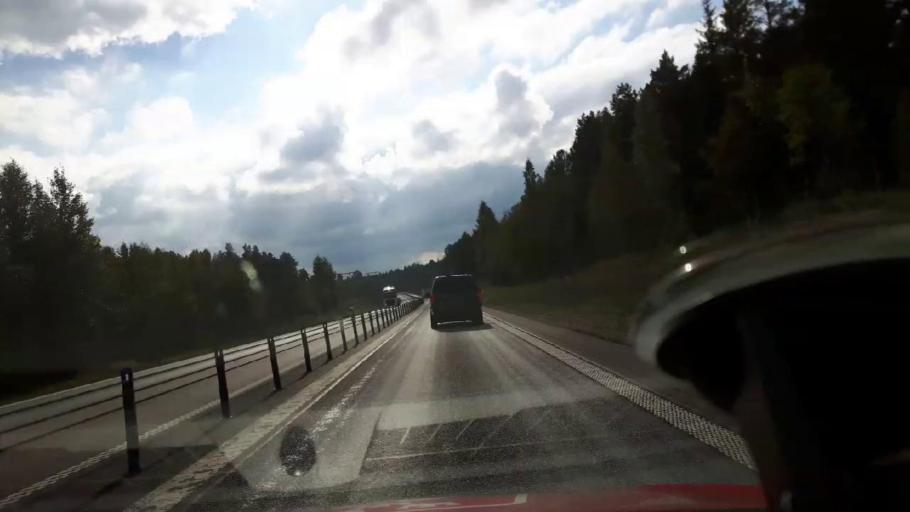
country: SE
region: Gaevleborg
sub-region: Gavle Kommun
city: Norrsundet
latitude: 60.9368
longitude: 17.0150
